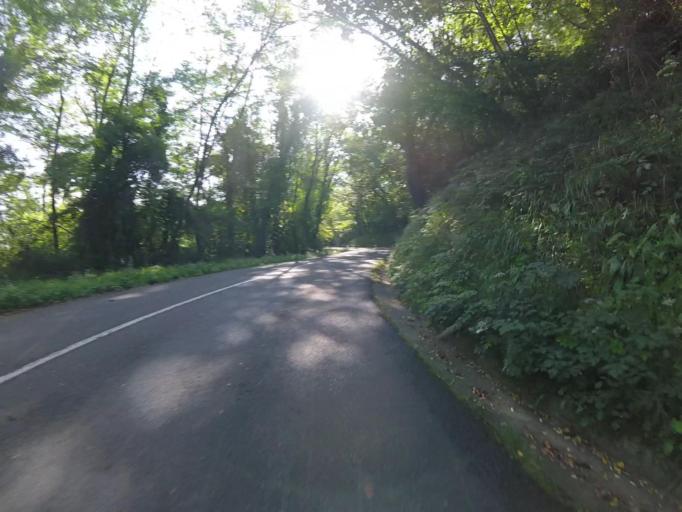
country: ES
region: Basque Country
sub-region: Provincia de Guipuzcoa
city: Irun
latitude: 43.3350
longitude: -1.7675
